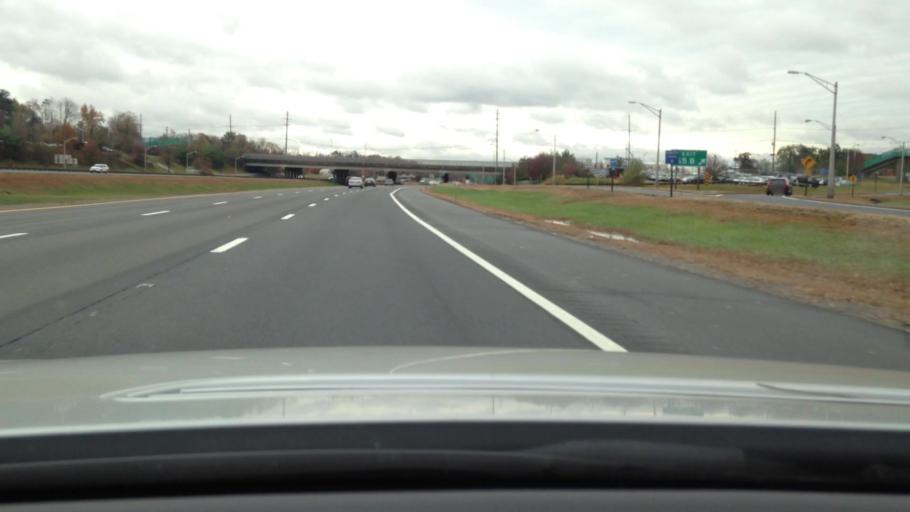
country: US
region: New Jersey
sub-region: Bergen County
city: Paramus
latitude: 40.9668
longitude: -74.0655
